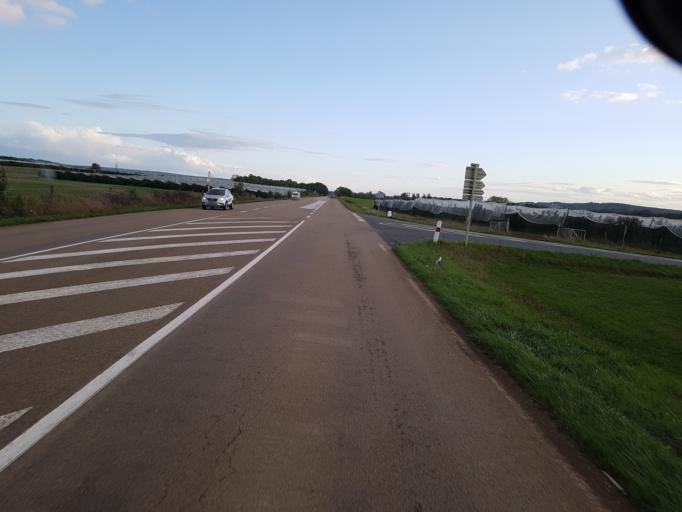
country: FR
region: Bourgogne
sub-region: Departement de l'Yonne
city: Saint-Clement
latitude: 48.2486
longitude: 3.2849
